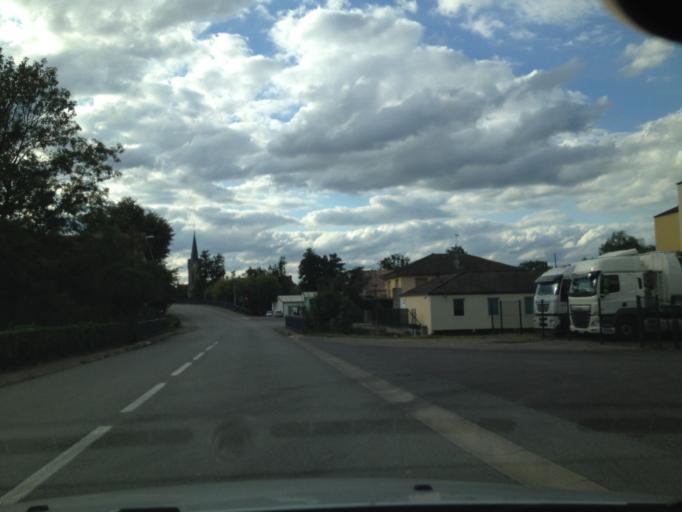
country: FR
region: Franche-Comte
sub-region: Departement de la Haute-Saone
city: Jussey
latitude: 47.9166
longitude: 5.9978
